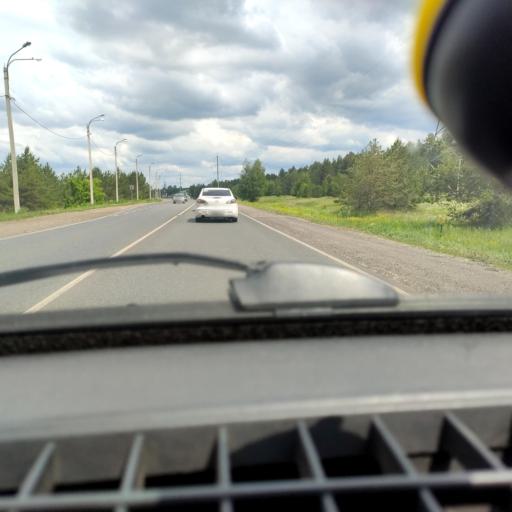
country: RU
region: Samara
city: Zhigulevsk
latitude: 53.5626
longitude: 49.5432
